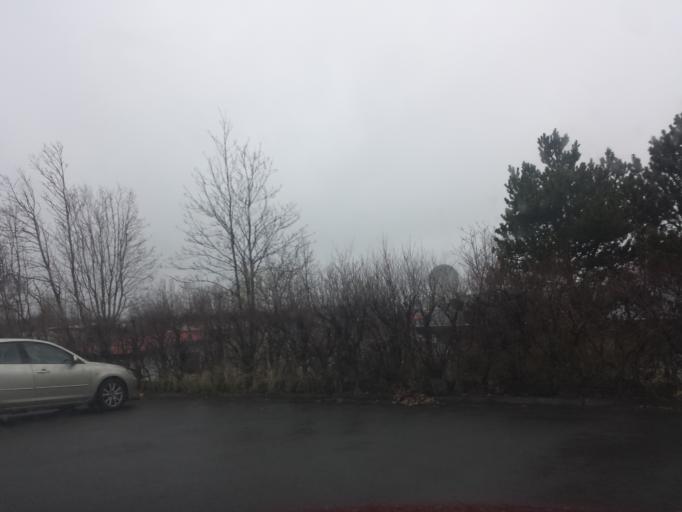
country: IS
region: Capital Region
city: Reykjavik
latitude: 64.1117
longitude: -21.8558
